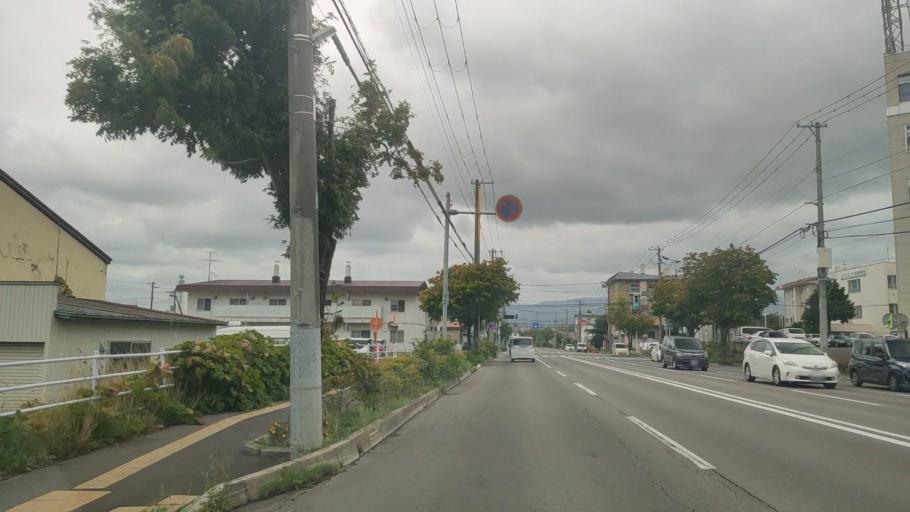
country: JP
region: Hokkaido
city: Hakodate
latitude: 41.7957
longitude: 140.7513
